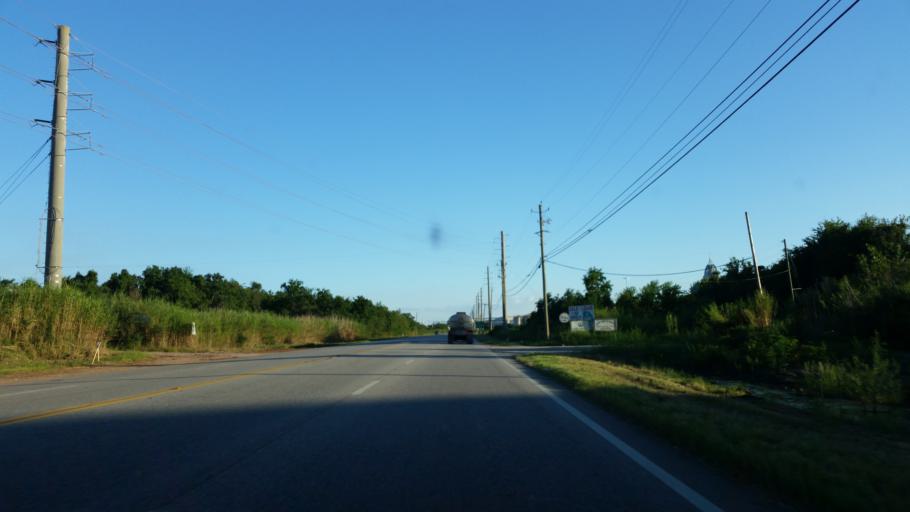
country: US
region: Alabama
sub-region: Mobile County
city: Mobile
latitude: 30.7135
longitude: -88.0336
